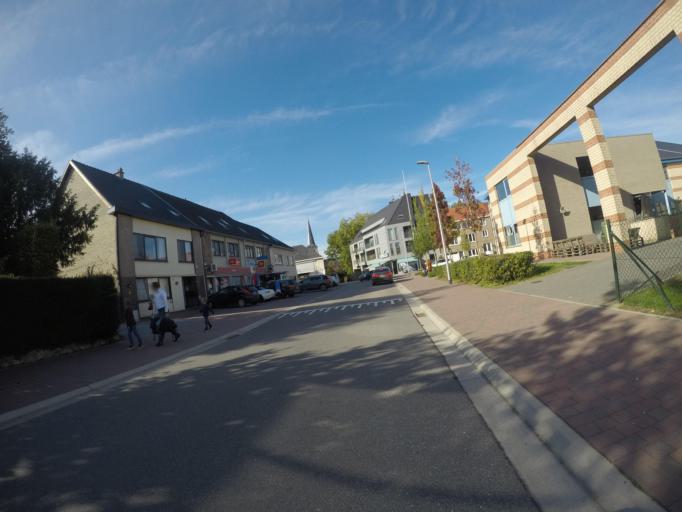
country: BE
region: Flanders
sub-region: Provincie Limburg
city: Diepenbeek
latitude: 50.9062
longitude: 5.4223
